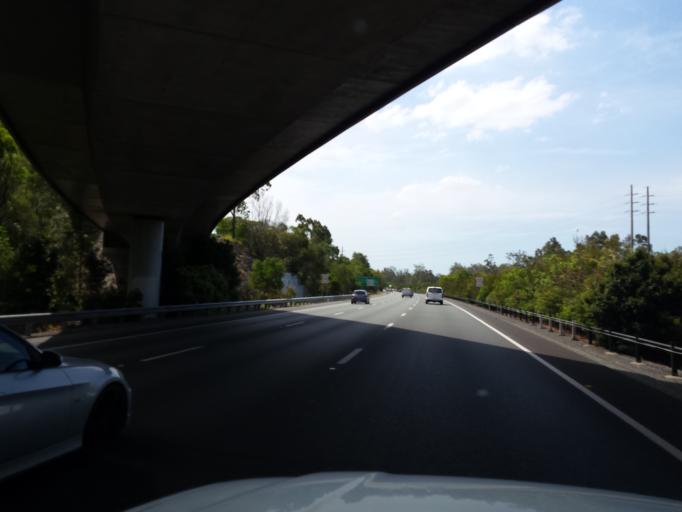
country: AU
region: Queensland
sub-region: Gold Coast
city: Nerang
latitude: -27.9597
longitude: 153.3451
